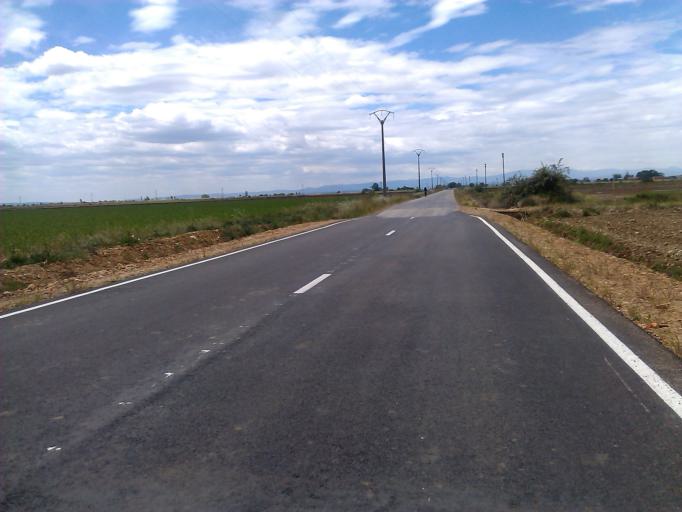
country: ES
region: Castille and Leon
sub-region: Provincia de Leon
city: Bustillo del Paramo
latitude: 42.4667
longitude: -5.7811
